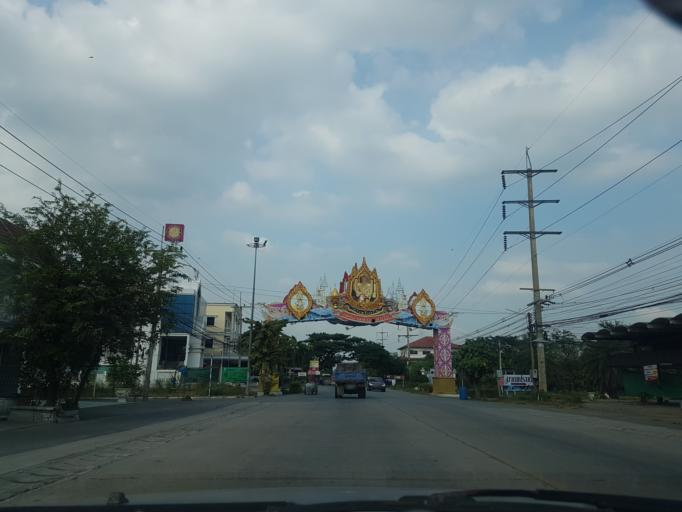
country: TH
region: Phra Nakhon Si Ayutthaya
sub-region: Amphoe Tha Ruea
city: Tha Ruea
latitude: 14.5698
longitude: 100.7259
